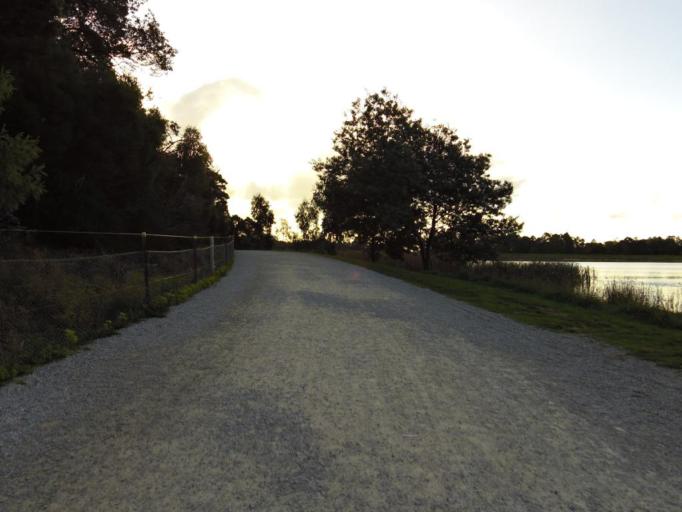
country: AU
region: Victoria
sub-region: Yarra Ranges
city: Lilydale
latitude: -37.7664
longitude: 145.3514
